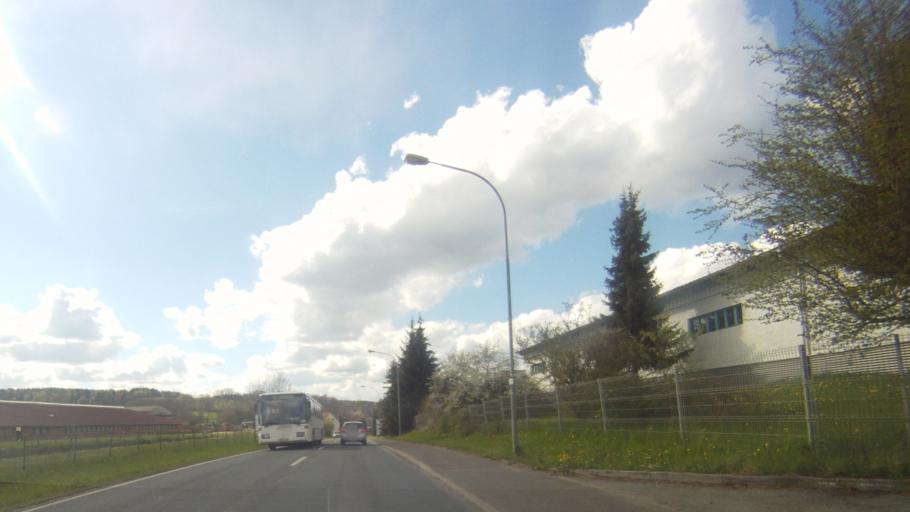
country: DE
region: Thuringia
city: Mengersgereuth-Hammern
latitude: 50.3815
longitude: 11.0659
